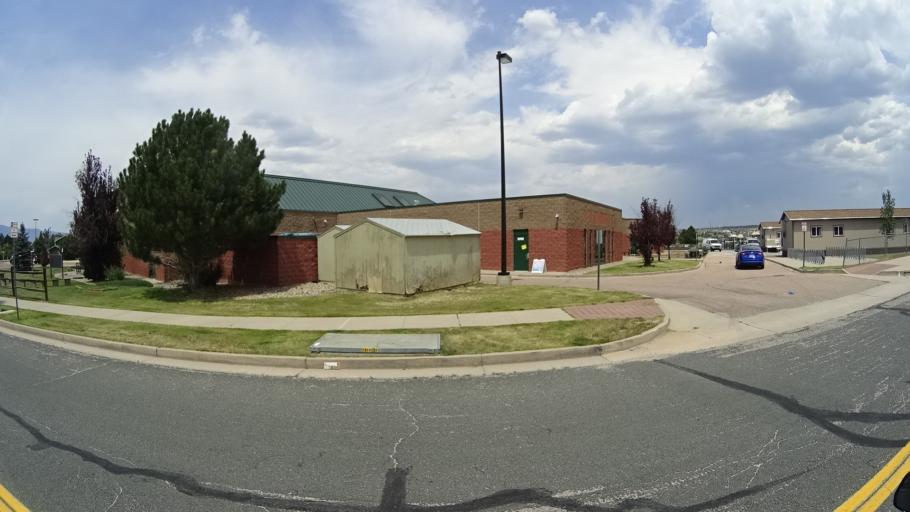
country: US
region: Colorado
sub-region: El Paso County
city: Black Forest
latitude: 38.9620
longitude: -104.7656
